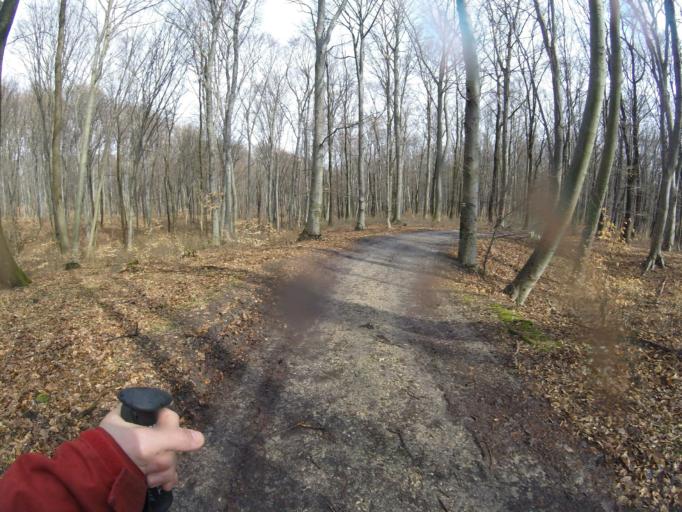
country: HU
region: Veszprem
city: Zirc
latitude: 47.3251
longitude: 17.8945
